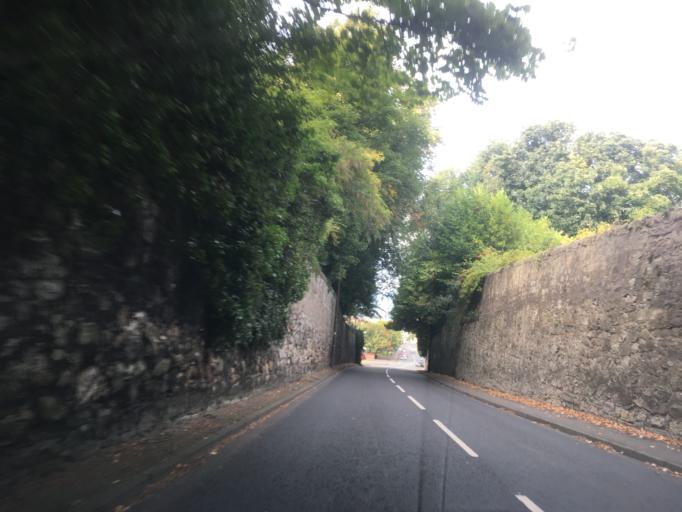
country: GB
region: Scotland
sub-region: East Lothian
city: Musselburgh
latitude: 55.9372
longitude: -3.0475
